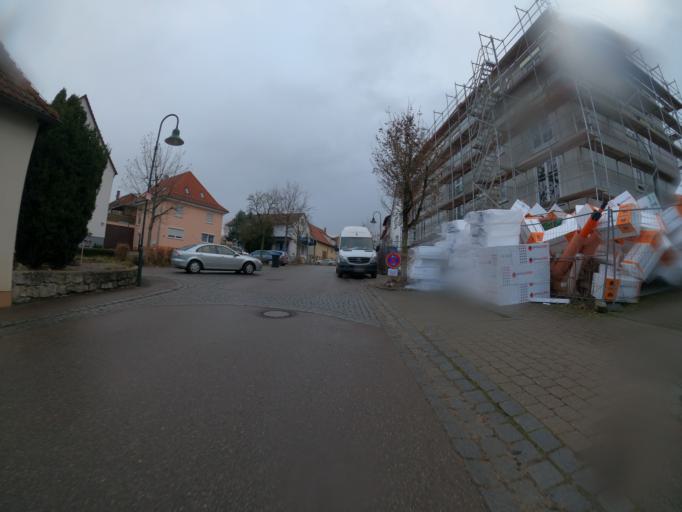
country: DE
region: Baden-Wuerttemberg
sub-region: Regierungsbezirk Stuttgart
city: Waschenbeuren
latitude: 48.7584
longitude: 9.6855
